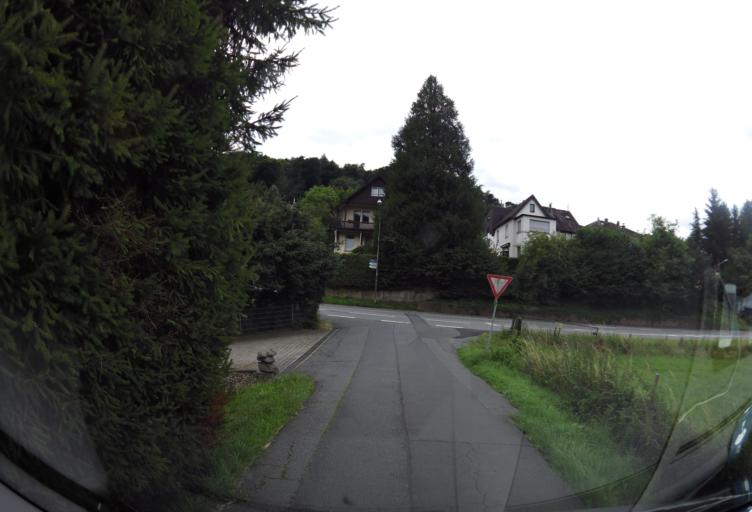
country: DE
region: Hesse
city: Ober-Ramstadt
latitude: 49.8289
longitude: 8.7094
